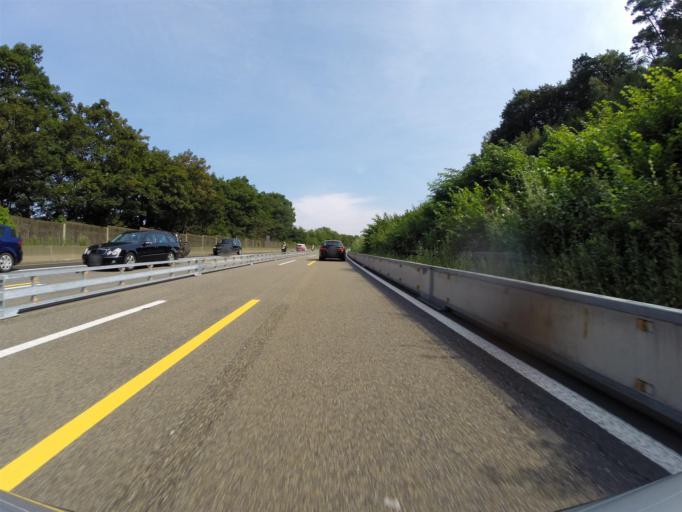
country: DE
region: Hesse
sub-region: Regierungsbezirk Kassel
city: Homberg
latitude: 50.9979
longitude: 9.4747
